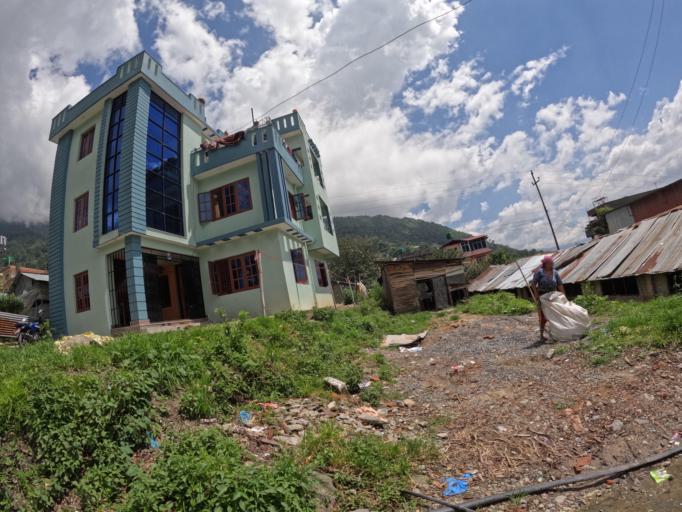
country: NP
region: Central Region
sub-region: Bagmati Zone
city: Kathmandu
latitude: 27.7951
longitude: 85.3302
